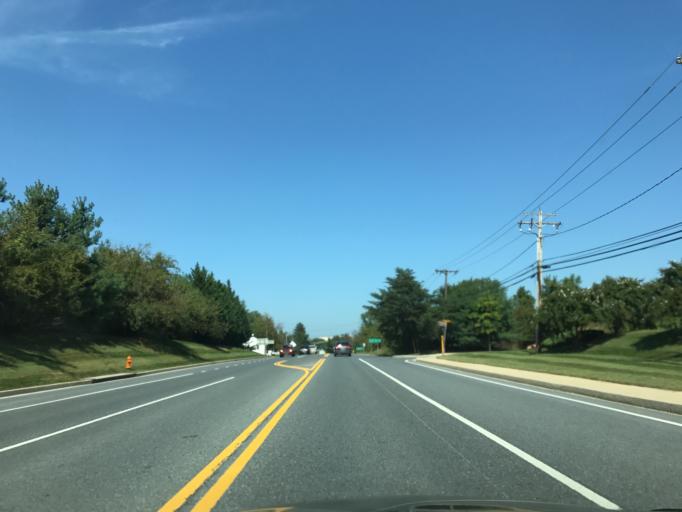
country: US
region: Maryland
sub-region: Howard County
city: Ilchester
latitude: 39.2027
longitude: -76.7953
